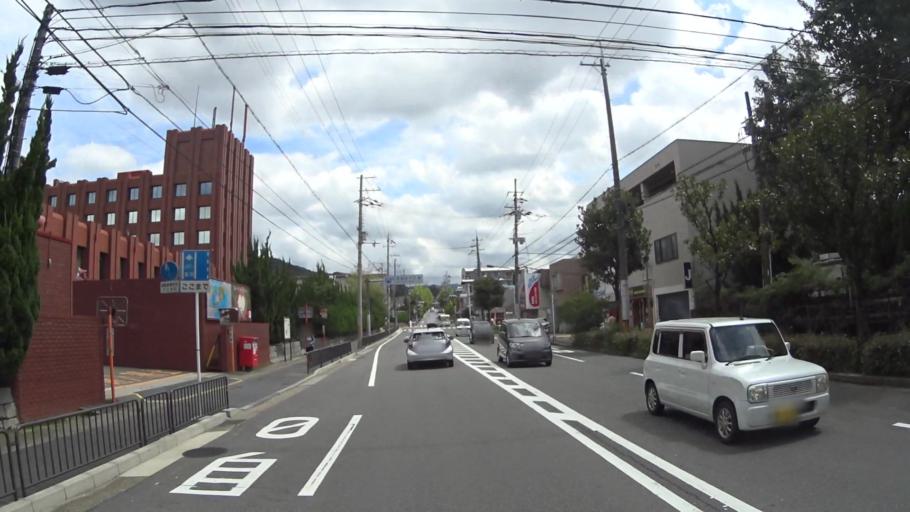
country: JP
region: Kyoto
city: Kyoto
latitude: 34.9632
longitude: 135.7670
